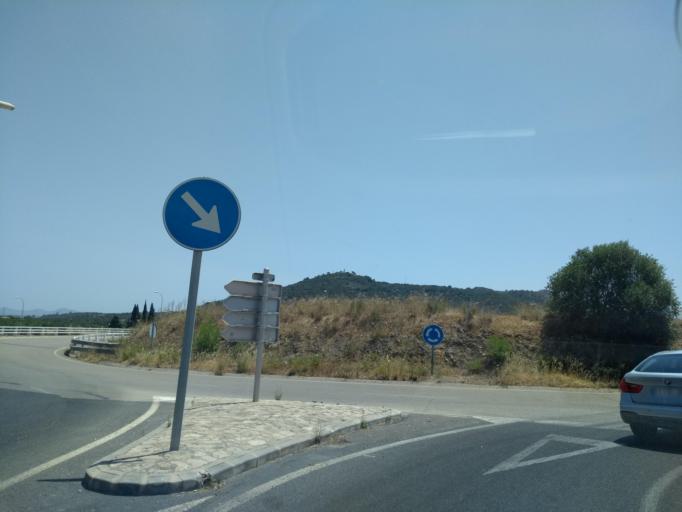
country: ES
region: Balearic Islands
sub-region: Illes Balears
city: Inca
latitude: 39.7350
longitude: 2.9386
